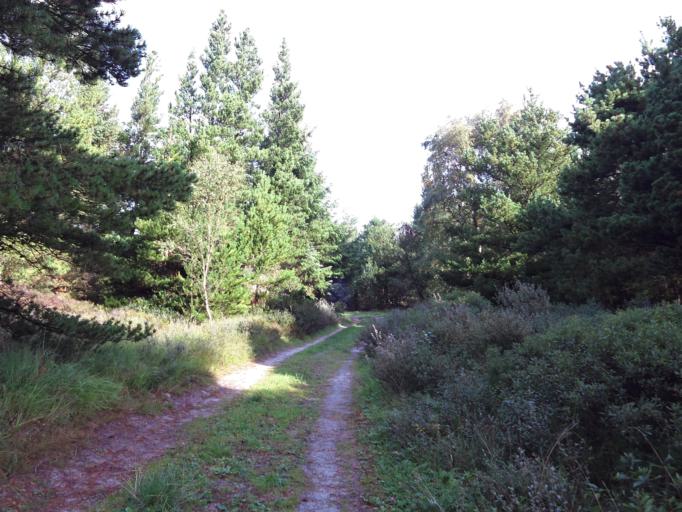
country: DK
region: South Denmark
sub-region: Varde Kommune
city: Oksbol
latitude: 55.5550
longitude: 8.2106
